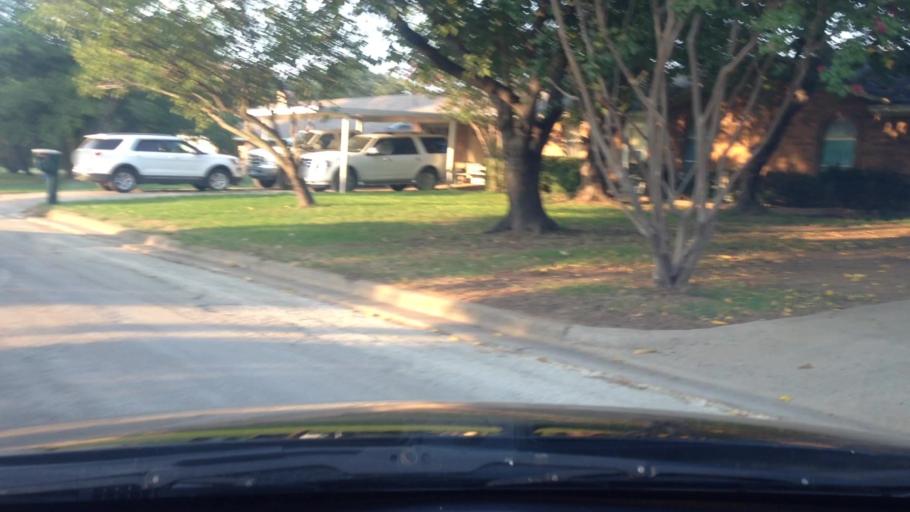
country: US
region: Texas
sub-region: Tarrant County
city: Rendon
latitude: 32.6035
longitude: -97.2412
